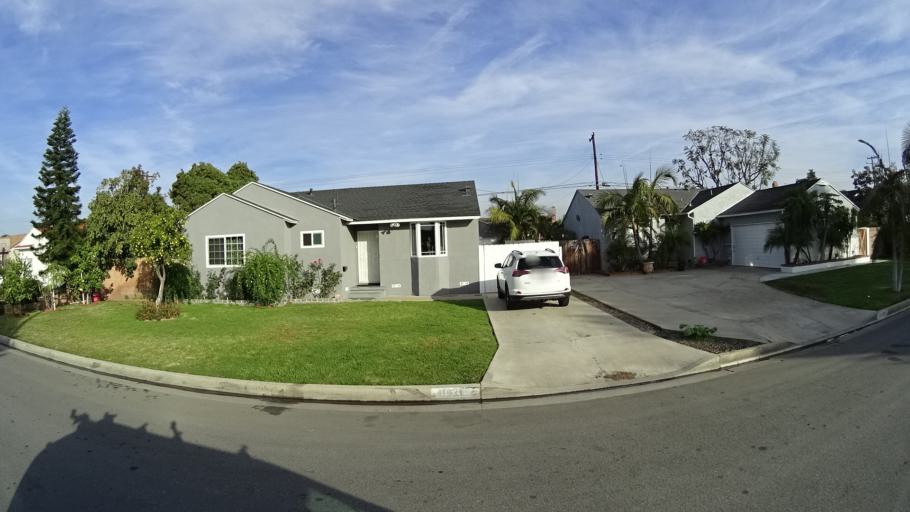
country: US
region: California
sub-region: Orange County
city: Garden Grove
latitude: 33.7929
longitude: -117.9304
